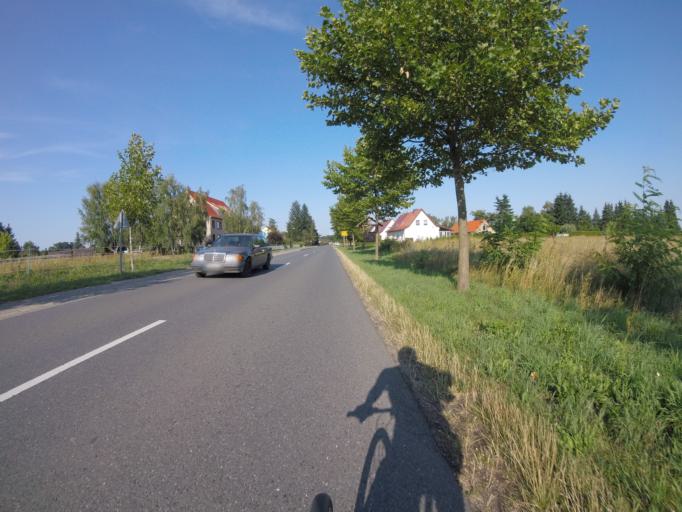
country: DE
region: Brandenburg
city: Bliesdorf
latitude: 52.6920
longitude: 14.1542
